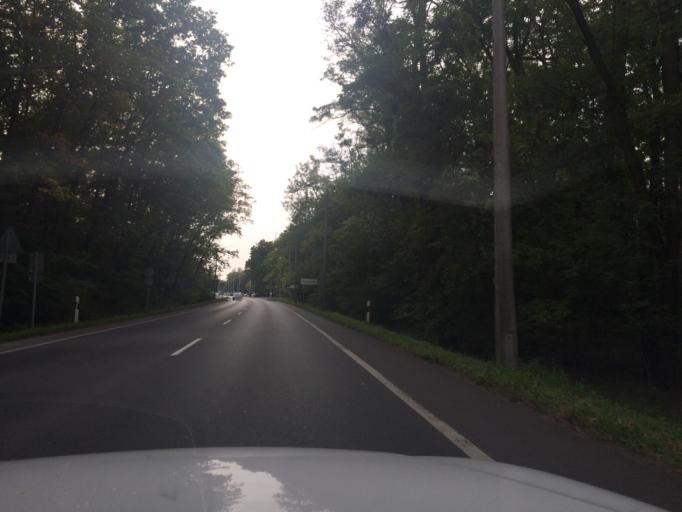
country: HU
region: Szabolcs-Szatmar-Bereg
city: Nyiregyhaza
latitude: 47.9814
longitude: 21.7176
